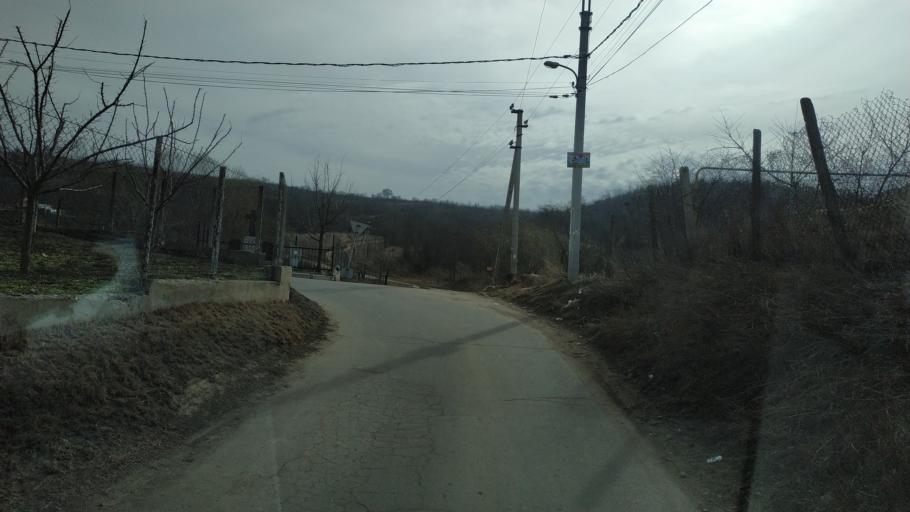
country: MD
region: Chisinau
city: Vatra
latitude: 47.0868
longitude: 28.7730
